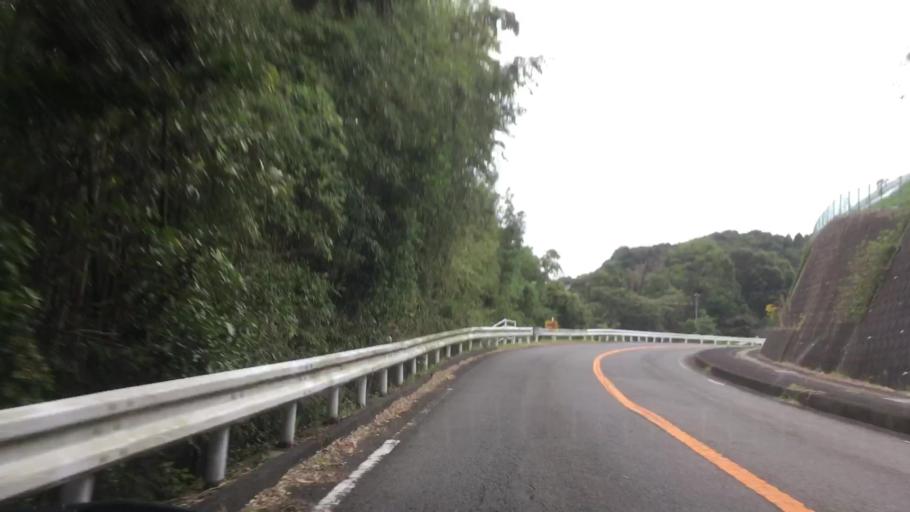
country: JP
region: Nagasaki
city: Sasebo
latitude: 32.9970
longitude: 129.7256
